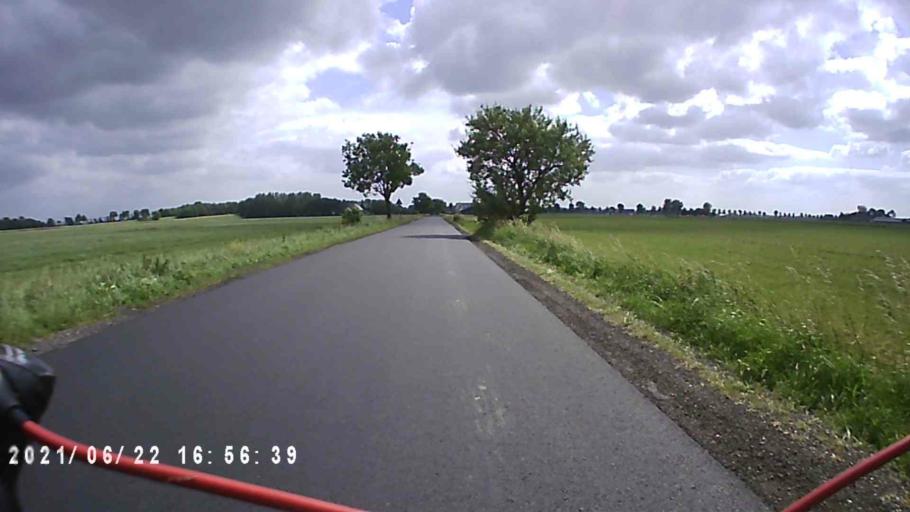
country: NL
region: Groningen
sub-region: Gemeente Bedum
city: Bedum
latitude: 53.3080
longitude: 6.6483
